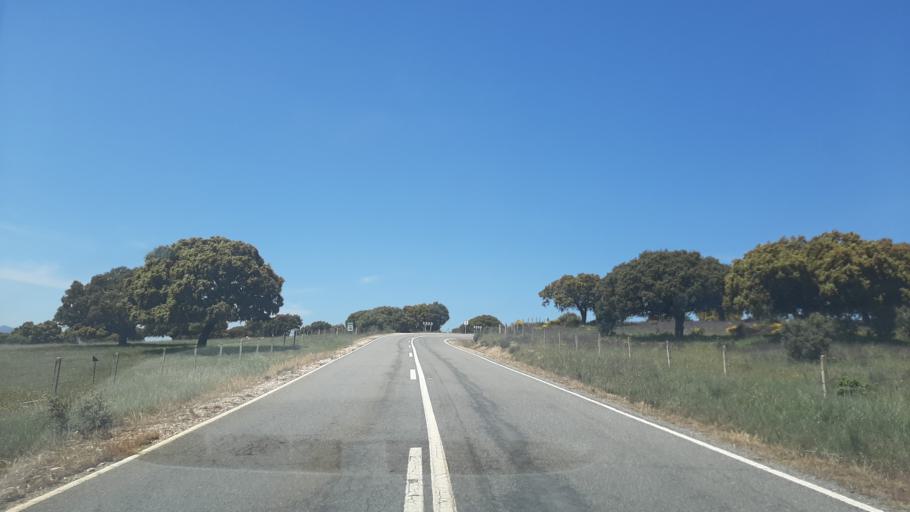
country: ES
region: Castille and Leon
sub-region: Provincia de Salamanca
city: Puente del Congosto
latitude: 40.5296
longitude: -5.5208
